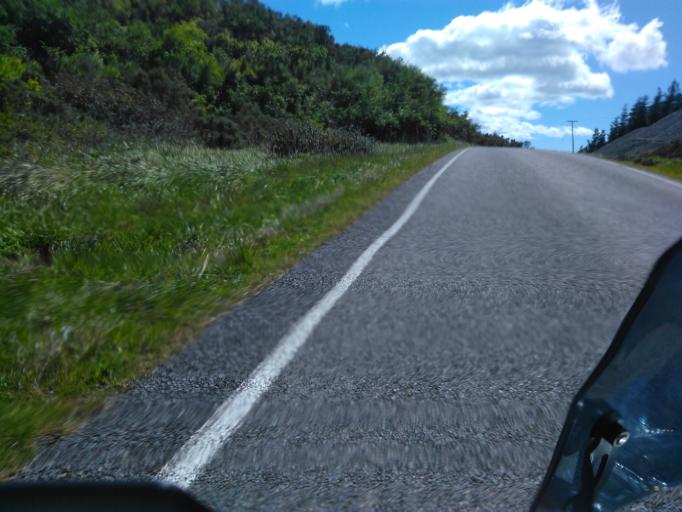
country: NZ
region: Gisborne
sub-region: Gisborne District
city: Gisborne
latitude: -38.5320
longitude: 178.2203
